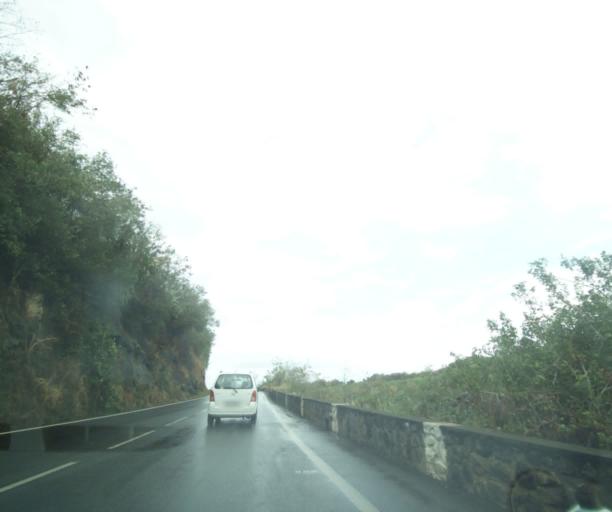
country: RE
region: Reunion
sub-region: Reunion
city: Saint-Paul
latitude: -21.0356
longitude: 55.2800
